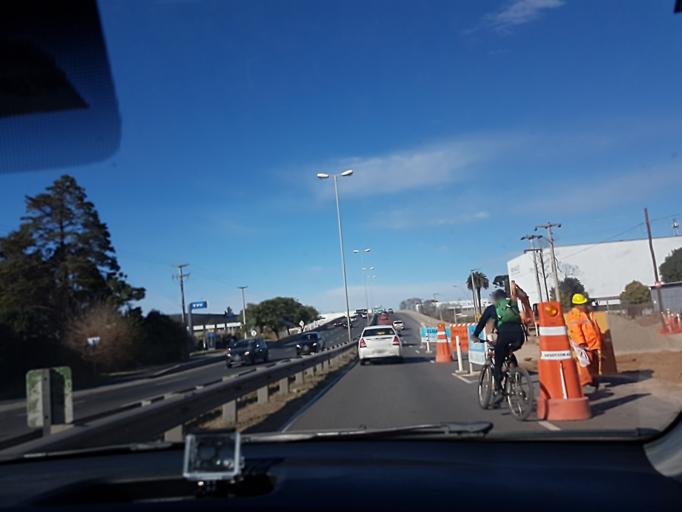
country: AR
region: Cordoba
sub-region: Departamento de Capital
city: Cordoba
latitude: -31.3409
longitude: -64.2079
